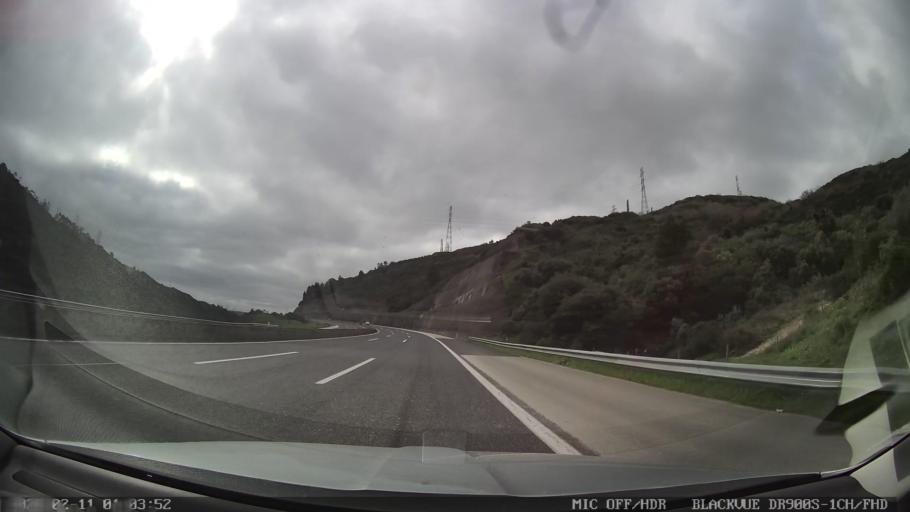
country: PT
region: Lisbon
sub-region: Loures
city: Bucelas
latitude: 38.8862
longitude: -9.1287
